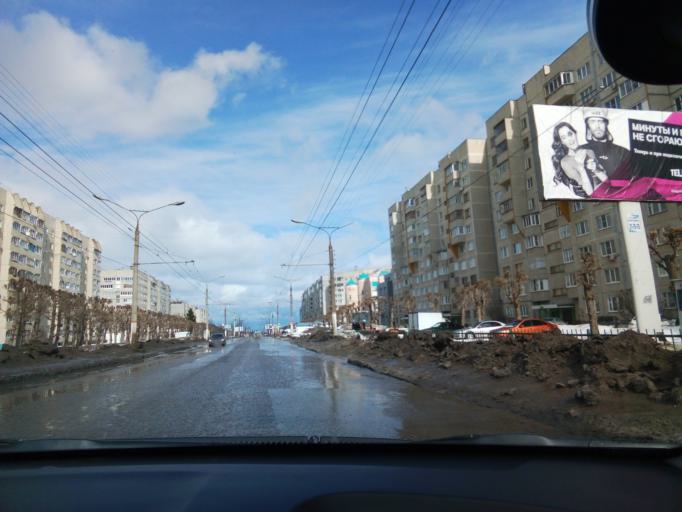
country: RU
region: Chuvashia
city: Novyye Lapsary
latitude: 56.1155
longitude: 47.1899
